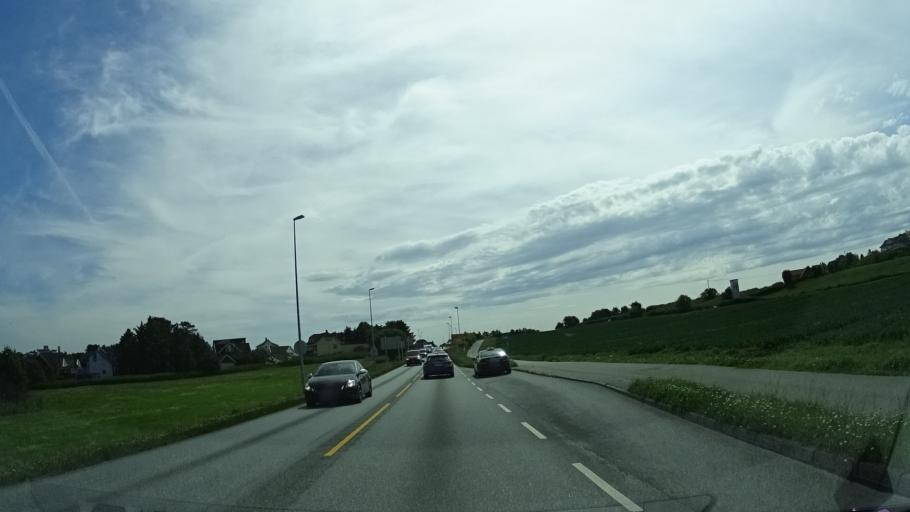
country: NO
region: Rogaland
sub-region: Randaberg
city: Randaberg
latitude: 59.0115
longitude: 5.6362
